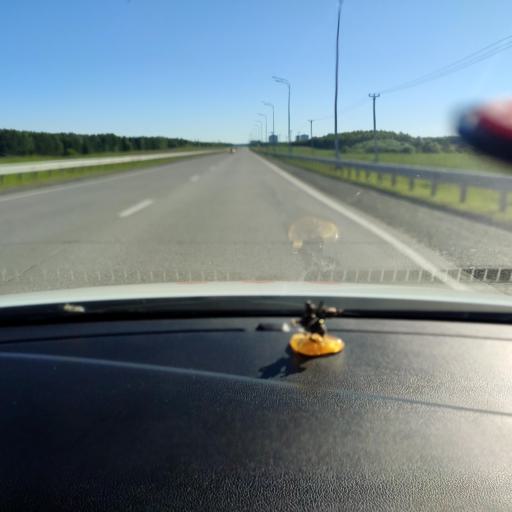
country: RU
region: Tatarstan
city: Stolbishchi
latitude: 55.6675
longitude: 49.1676
